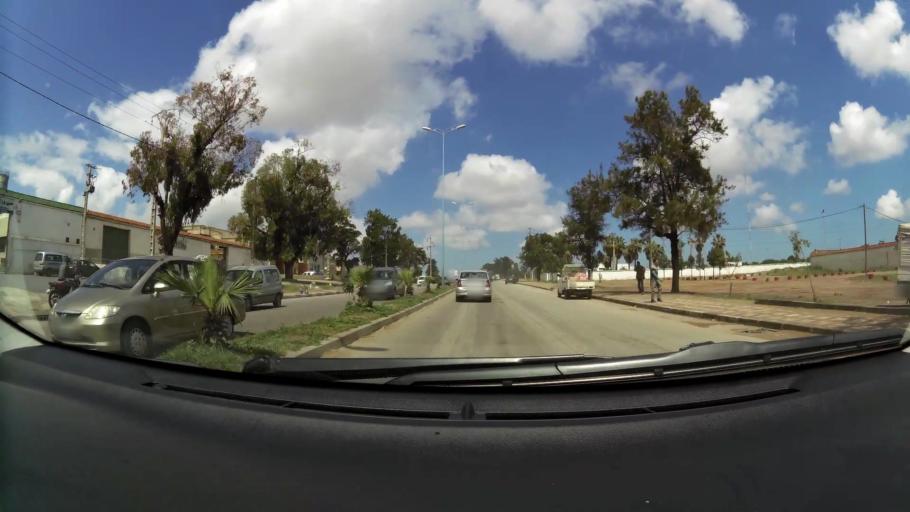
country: MA
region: Grand Casablanca
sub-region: Casablanca
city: Casablanca
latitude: 33.5314
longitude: -7.5695
